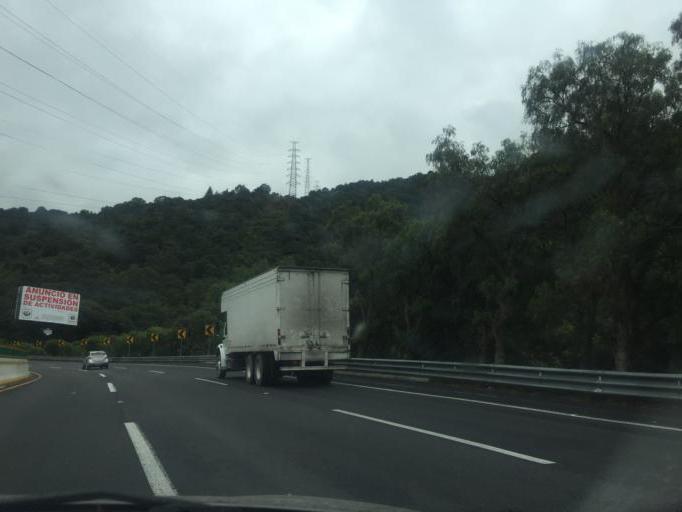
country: MX
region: Mexico City
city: Xochimilco
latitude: 19.2258
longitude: -99.1452
